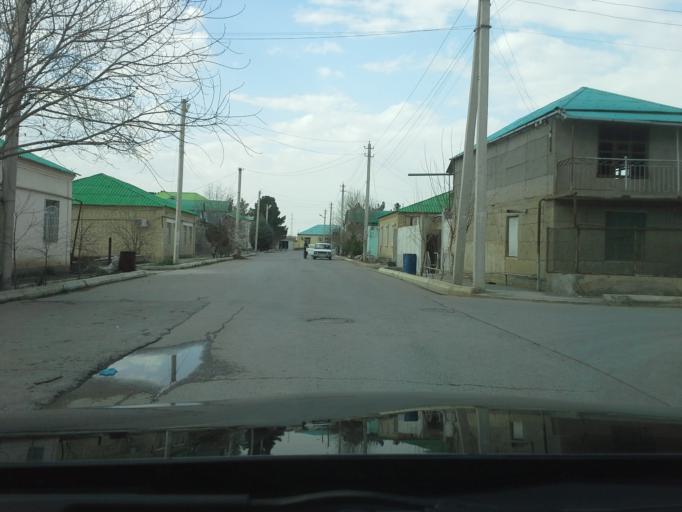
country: TM
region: Ahal
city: Abadan
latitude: 37.9880
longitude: 58.2797
